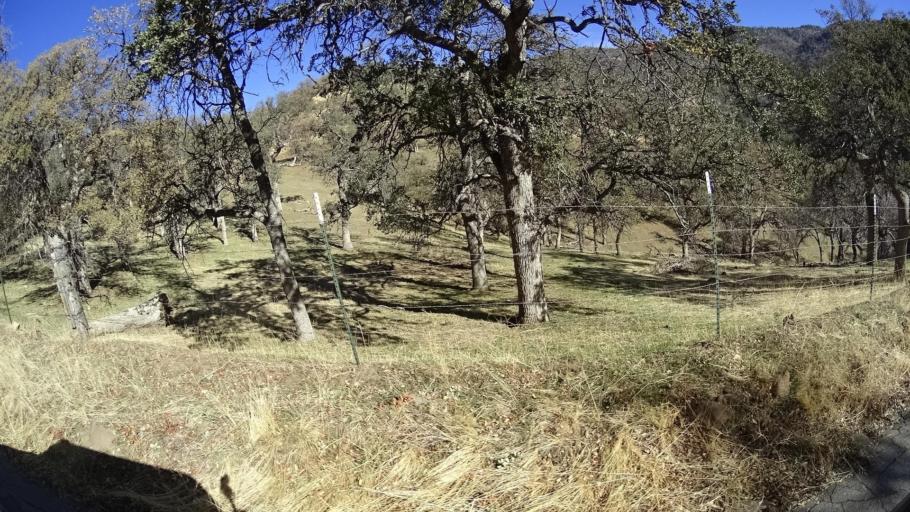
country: US
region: California
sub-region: Kern County
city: Bodfish
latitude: 35.4524
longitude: -118.6564
